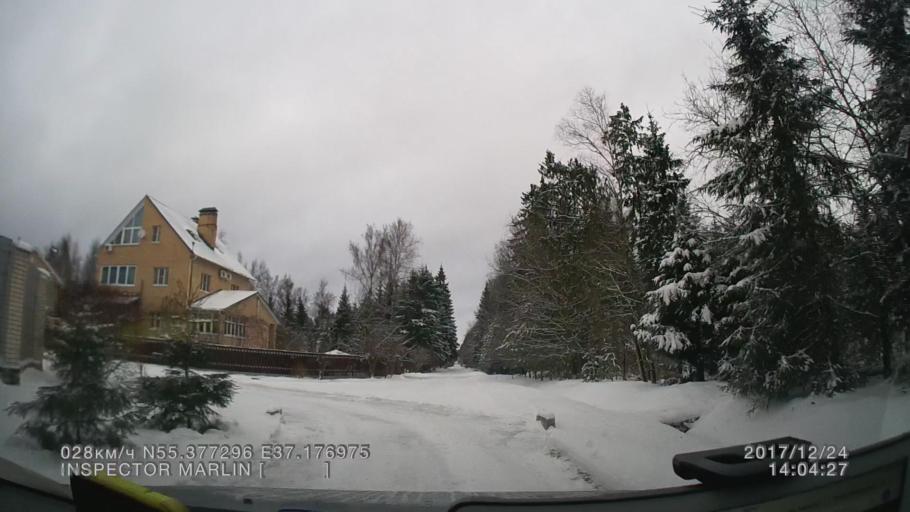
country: RU
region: Moskovskaya
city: Troitsk
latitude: 55.3774
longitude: 37.1770
